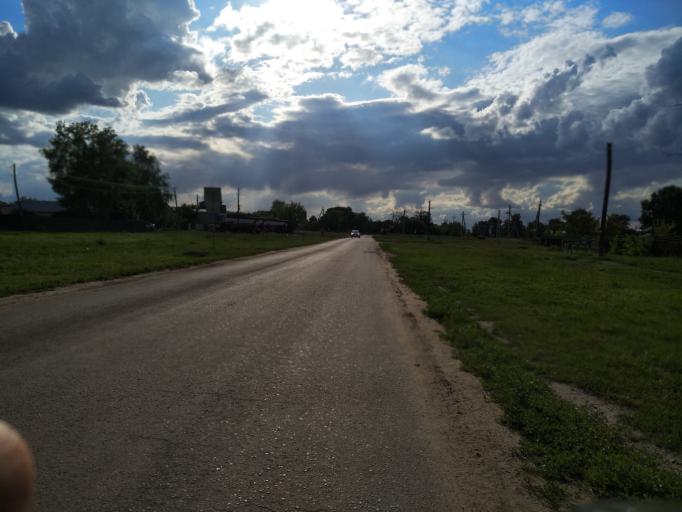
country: RU
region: Lipetsk
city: Dobrinka
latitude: 52.0383
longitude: 40.5438
